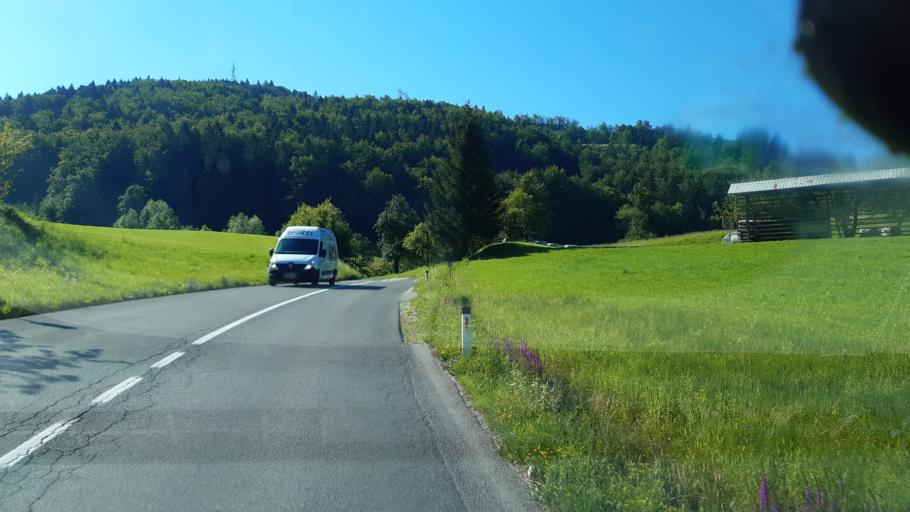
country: SI
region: Gornji Grad
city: Gornji Grad
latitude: 46.2176
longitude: 14.7925
